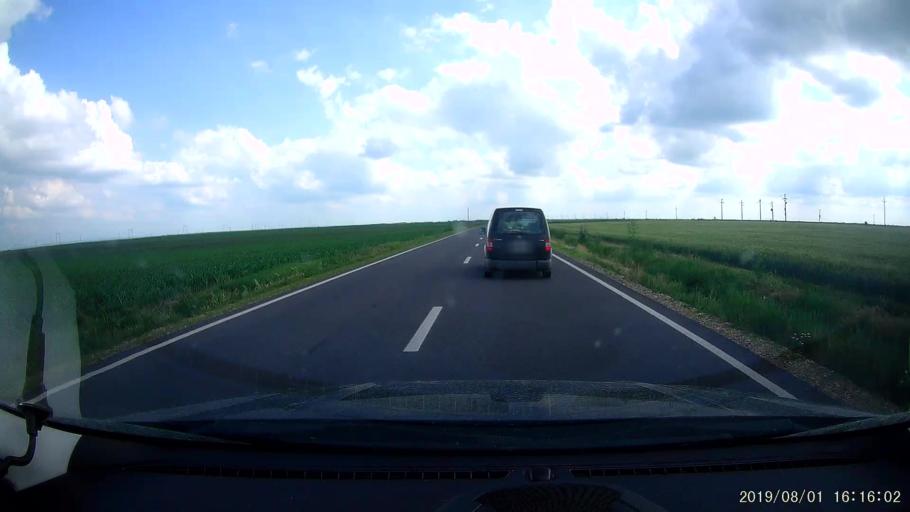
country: RO
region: Calarasi
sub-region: Comuna Stefan Voda
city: Stefan Voda
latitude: 44.3275
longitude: 27.3595
